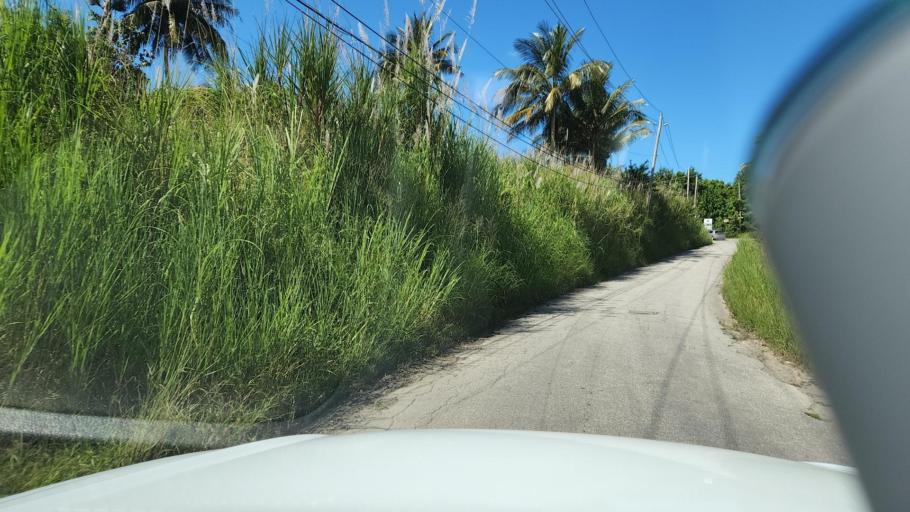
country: BB
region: Saint Thomas
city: Welchman Hall
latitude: 13.1968
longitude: -59.5659
